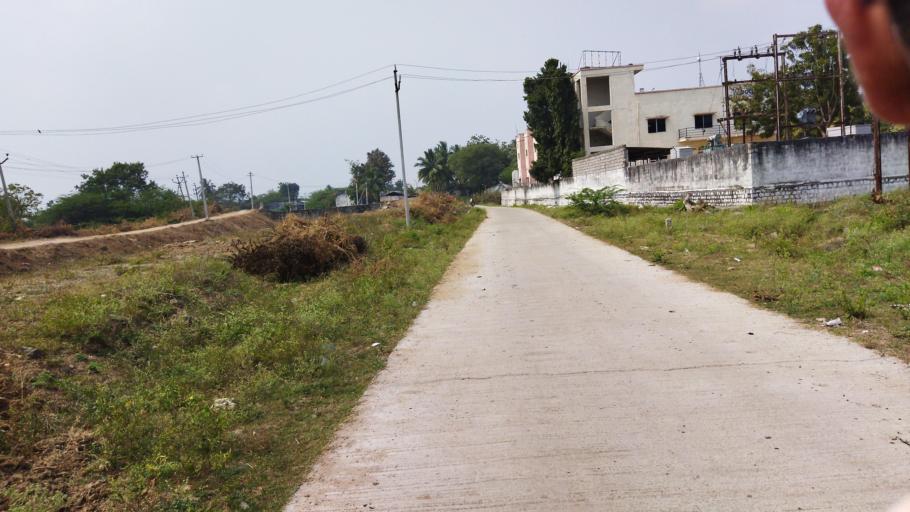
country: IN
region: Telangana
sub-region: Nalgonda
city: Nalgonda
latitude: 17.0843
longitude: 79.2755
